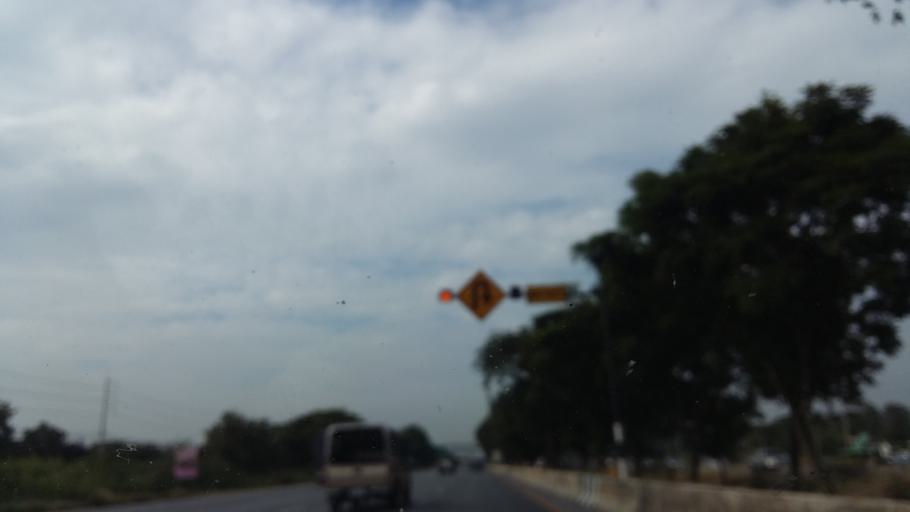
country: TH
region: Phra Nakhon Si Ayutthaya
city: Bang Pahan
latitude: 14.4904
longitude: 100.5257
